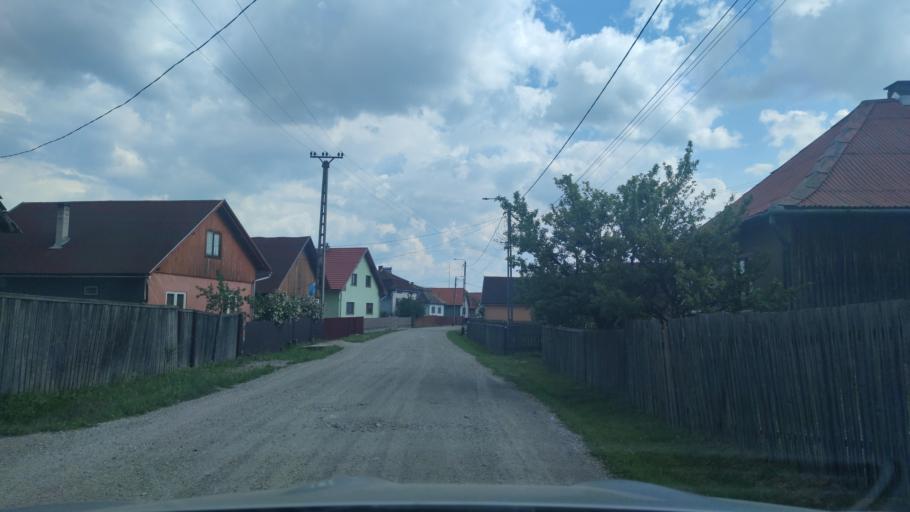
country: RO
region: Harghita
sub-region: Comuna Remetea
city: Remetea
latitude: 46.7985
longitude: 25.4438
